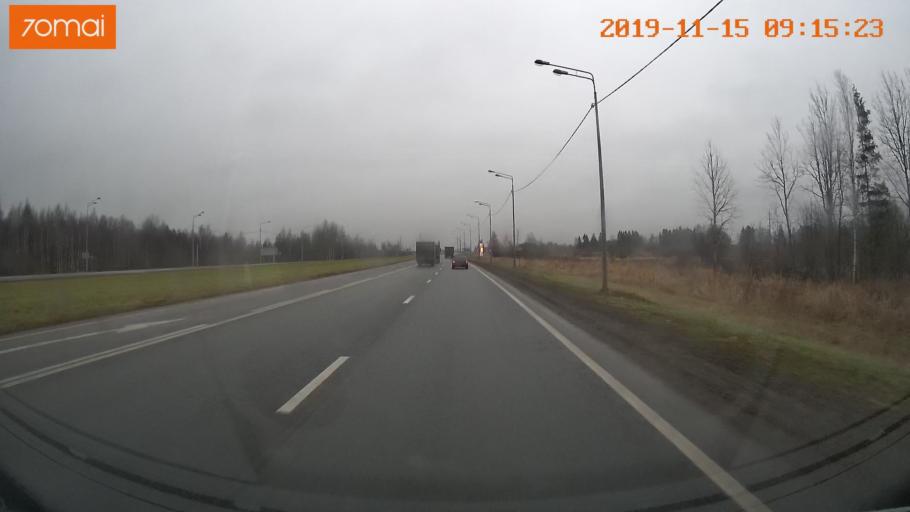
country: RU
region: Vologda
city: Tonshalovo
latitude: 59.2381
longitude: 37.9666
